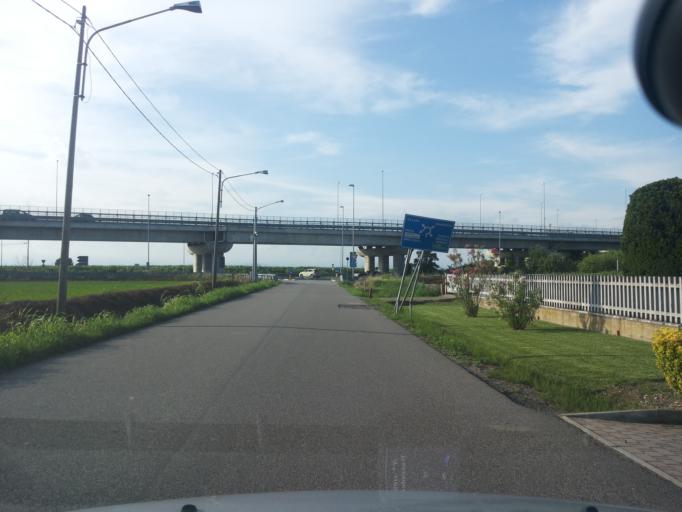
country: IT
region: Piedmont
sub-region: Provincia di Vercelli
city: Borgo Vercelli
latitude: 45.3630
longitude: 8.4607
